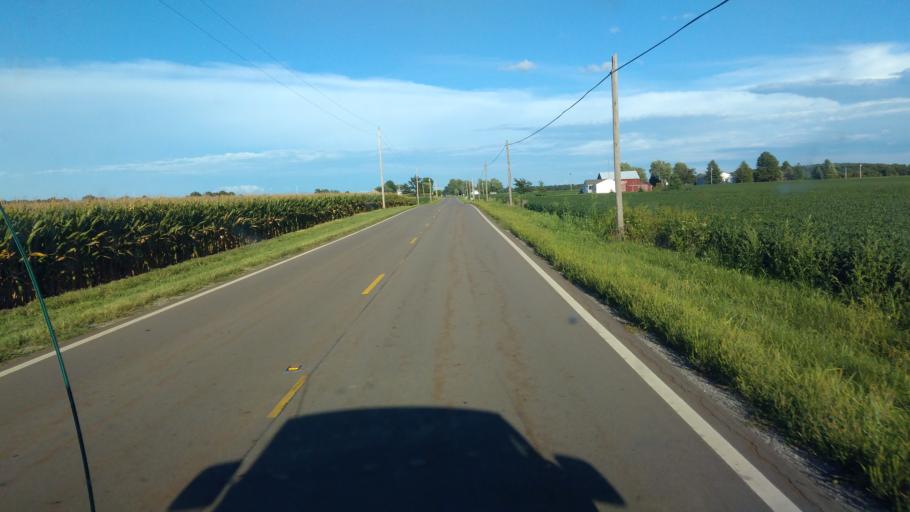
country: US
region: Ohio
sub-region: Hardin County
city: Forest
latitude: 40.8029
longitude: -83.4042
